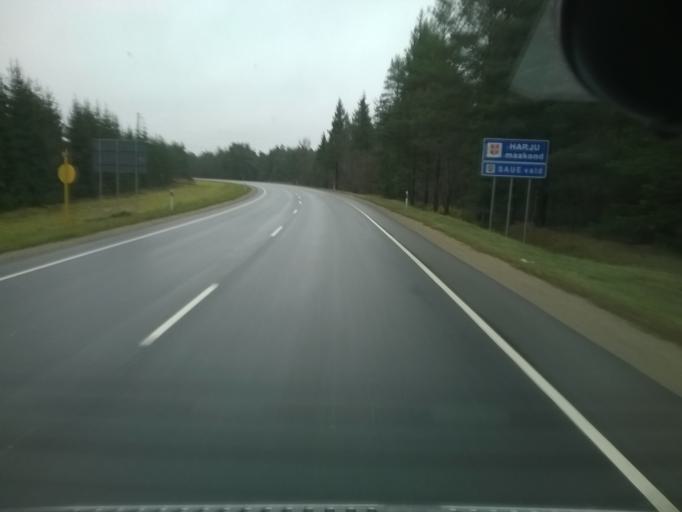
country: EE
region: Harju
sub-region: Nissi vald
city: Turba
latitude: 59.0358
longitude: 24.1652
